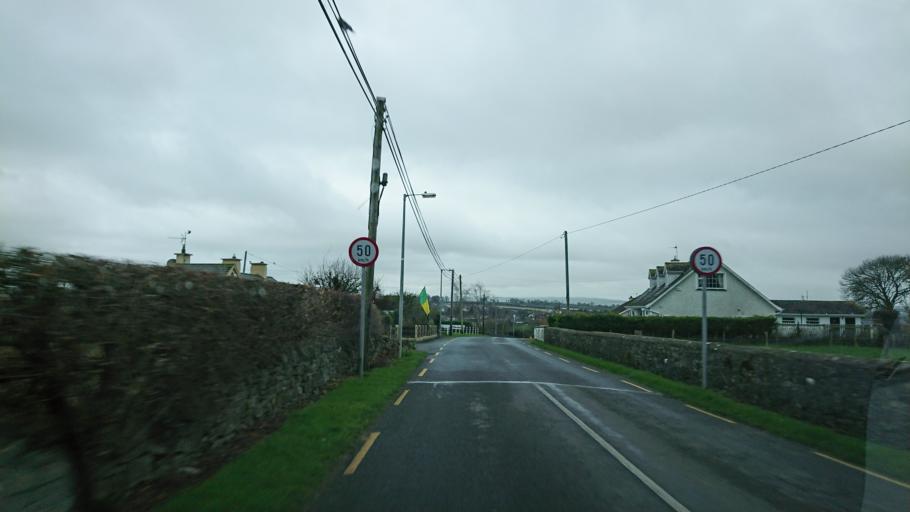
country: IE
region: Leinster
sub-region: Kilkenny
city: Kilkenny
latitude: 52.5455
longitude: -7.2722
